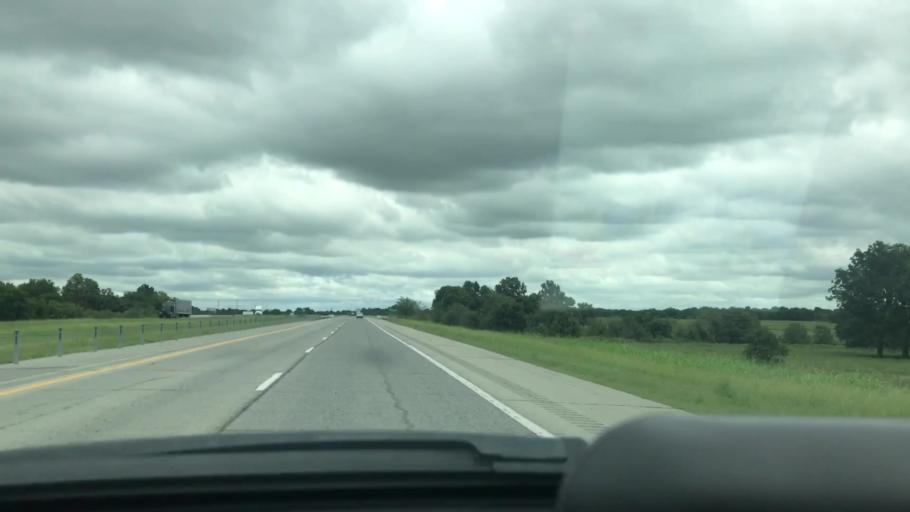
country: US
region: Oklahoma
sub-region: McIntosh County
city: Checotah
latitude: 35.5490
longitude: -95.4997
